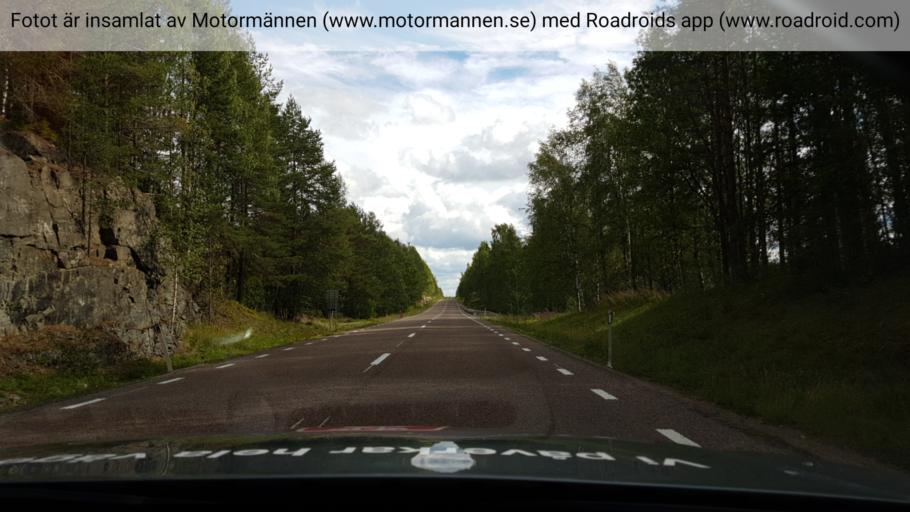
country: SE
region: Jaemtland
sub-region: OEstersunds Kommun
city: Brunflo
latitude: 63.1945
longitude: 15.1387
